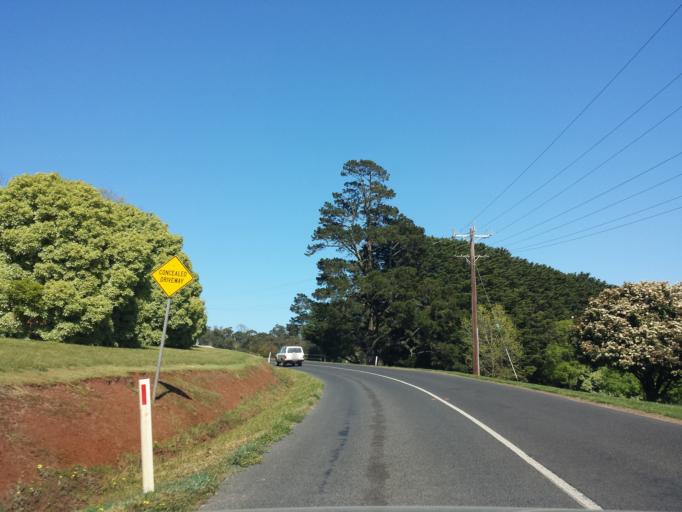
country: AU
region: Victoria
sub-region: Yarra Ranges
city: Woori Yallock
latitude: -37.8000
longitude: 145.4720
